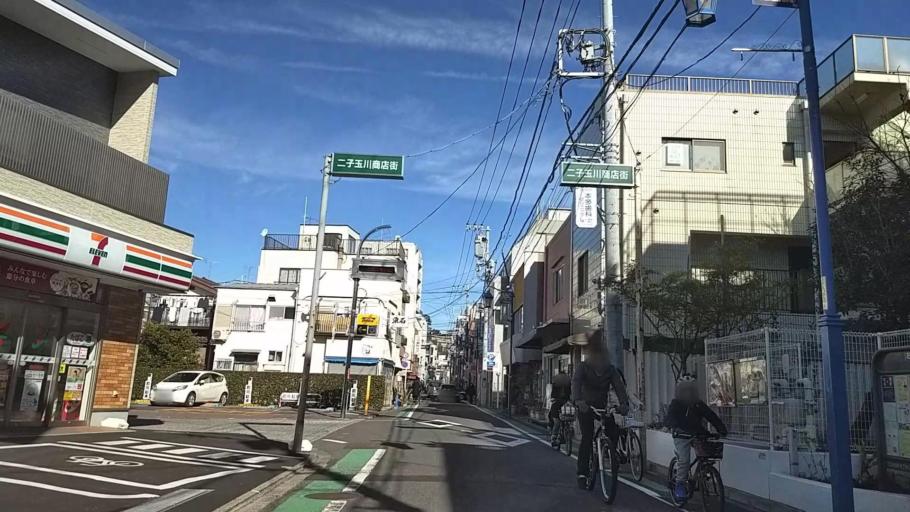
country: JP
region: Tokyo
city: Chofugaoka
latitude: 35.6164
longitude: 139.6256
